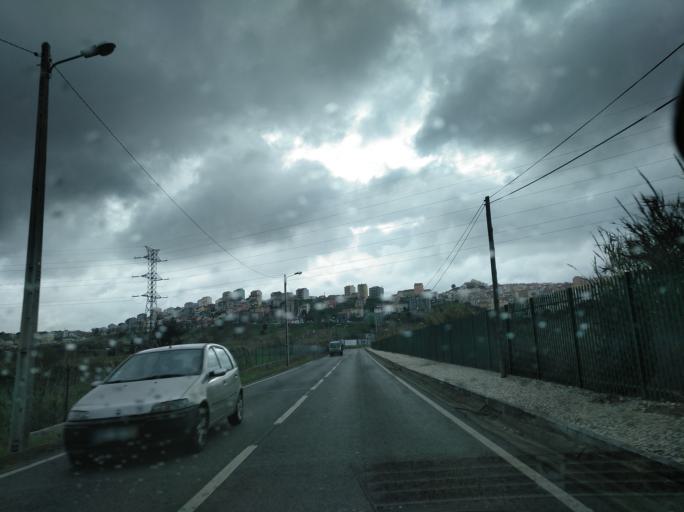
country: PT
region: Lisbon
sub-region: Odivelas
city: Pontinha
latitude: 38.7741
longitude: -9.2090
